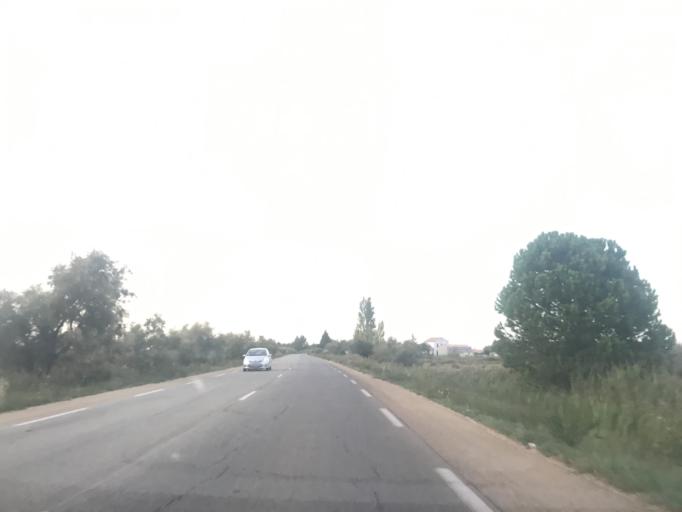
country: FR
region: Provence-Alpes-Cote d'Azur
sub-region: Departement des Bouches-du-Rhone
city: Saintes-Maries-de-la-Mer
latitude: 43.5215
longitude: 4.3998
